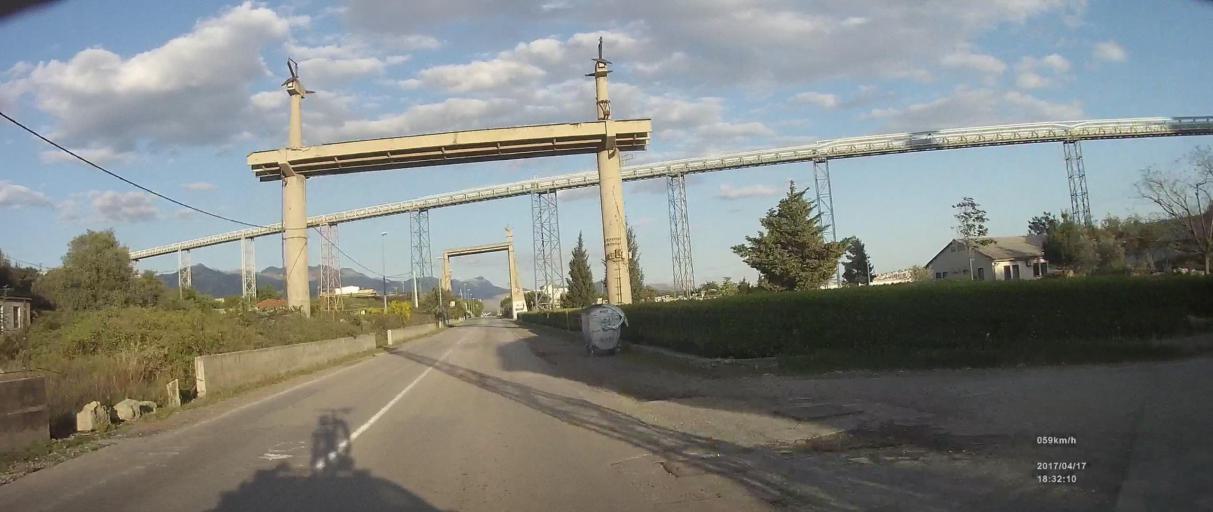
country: HR
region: Splitsko-Dalmatinska
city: Vranjic
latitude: 43.5432
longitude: 16.4425
